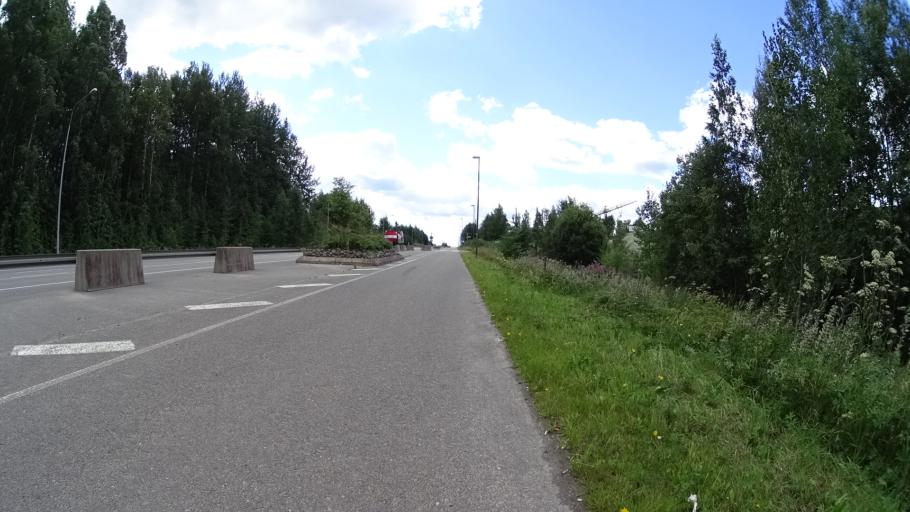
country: FI
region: Uusimaa
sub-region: Helsinki
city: Vantaa
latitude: 60.3261
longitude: 24.9195
